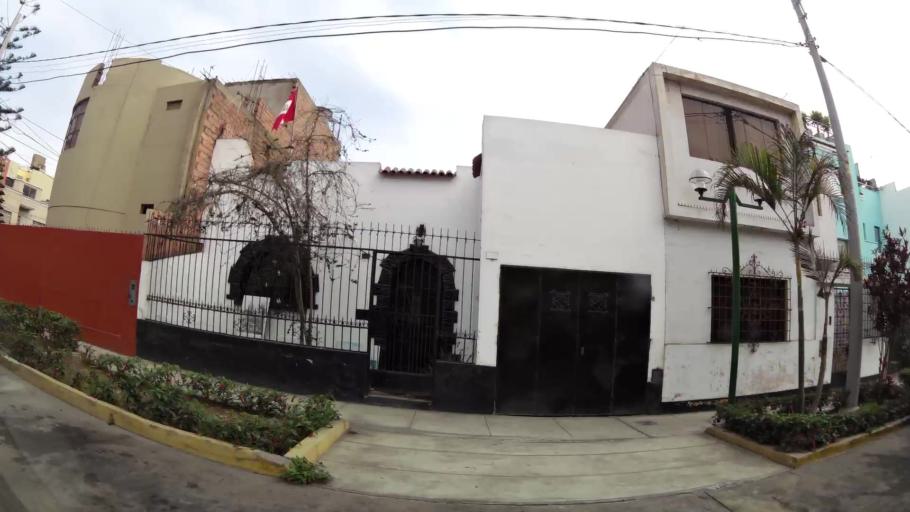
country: PE
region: Lima
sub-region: Lima
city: San Isidro
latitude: -12.0805
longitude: -77.0542
